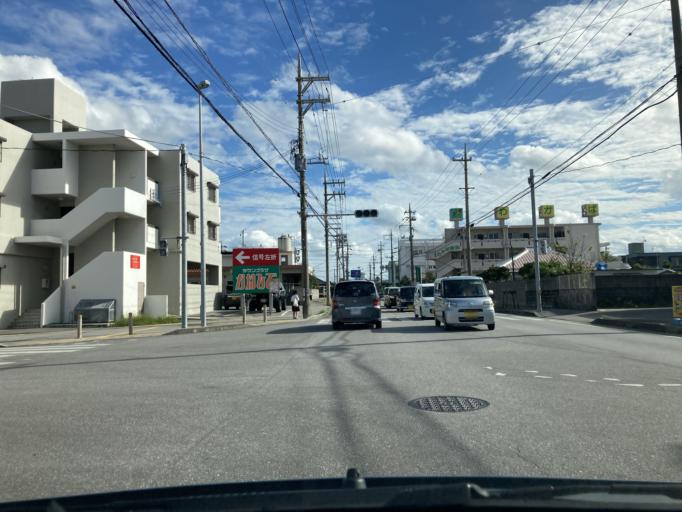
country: JP
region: Okinawa
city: Ishikawa
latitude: 26.4135
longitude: 127.8238
